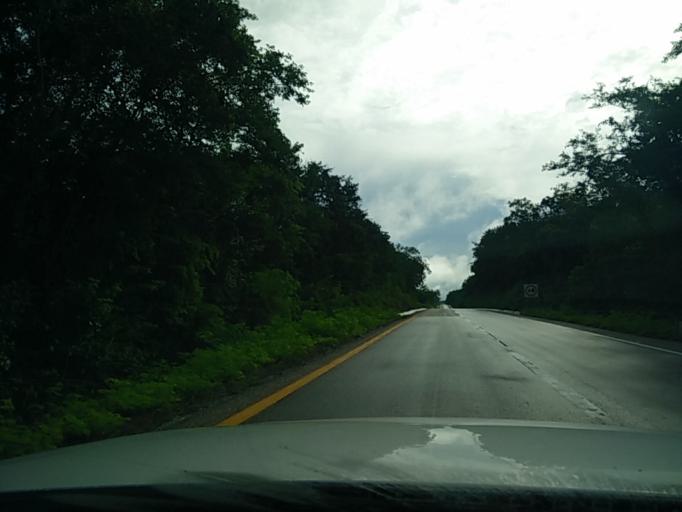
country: MX
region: Yucatan
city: Tunkas
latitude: 20.7642
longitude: -88.7947
